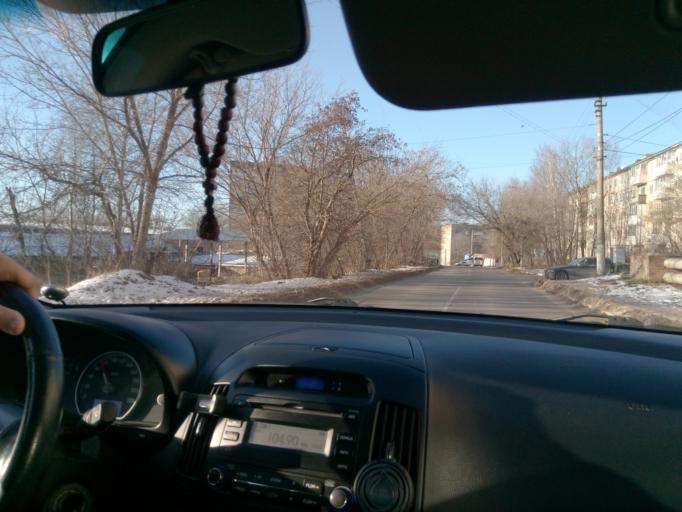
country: RU
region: Tula
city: Mendeleyevskiy
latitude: 54.1637
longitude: 37.5663
